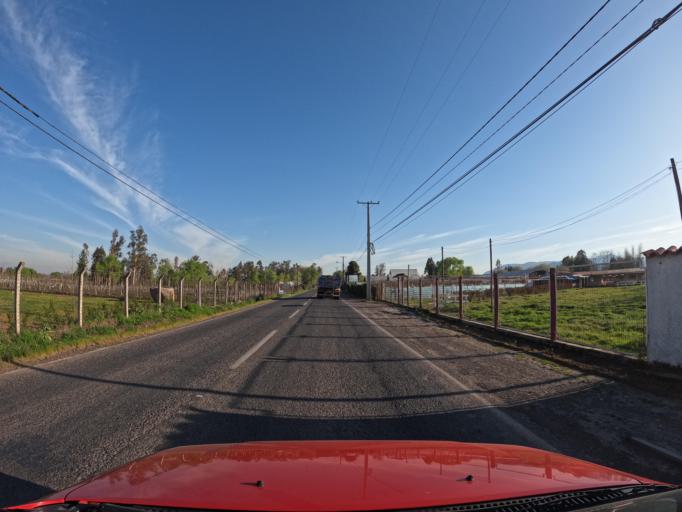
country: CL
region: Maule
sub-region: Provincia de Curico
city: Rauco
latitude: -34.8794
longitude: -71.2693
